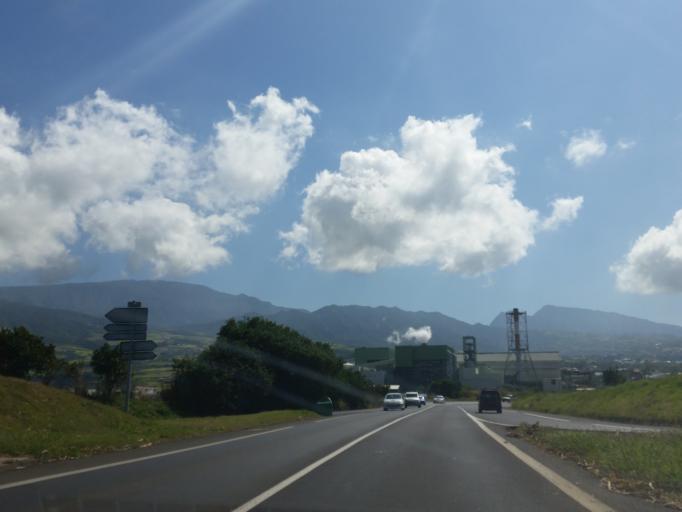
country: RE
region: Reunion
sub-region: Reunion
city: Saint-Louis
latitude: -21.2843
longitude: 55.3952
